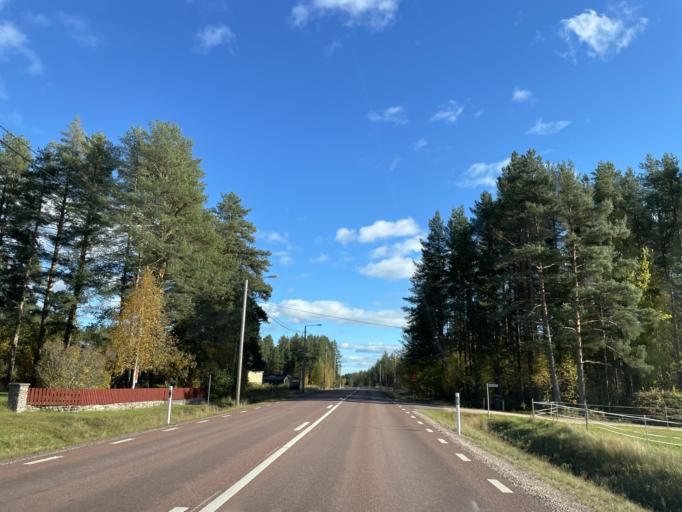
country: SE
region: Dalarna
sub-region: Malung-Saelens kommun
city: Malung
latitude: 60.7316
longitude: 13.5666
